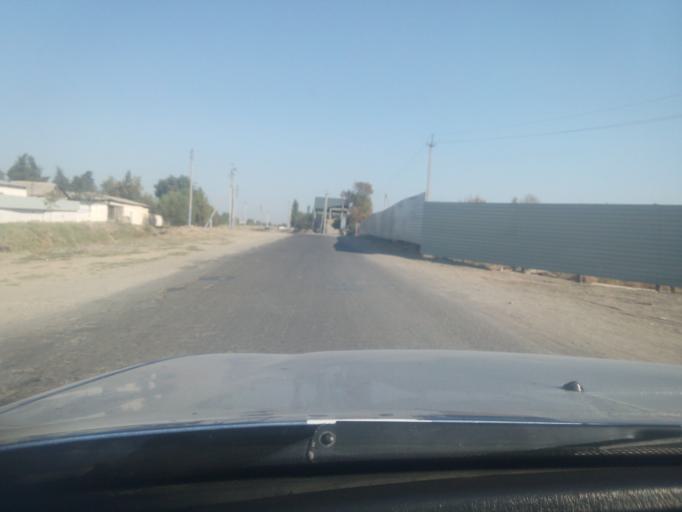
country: UZ
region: Sirdaryo
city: Guliston
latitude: 40.4950
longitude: 68.8005
